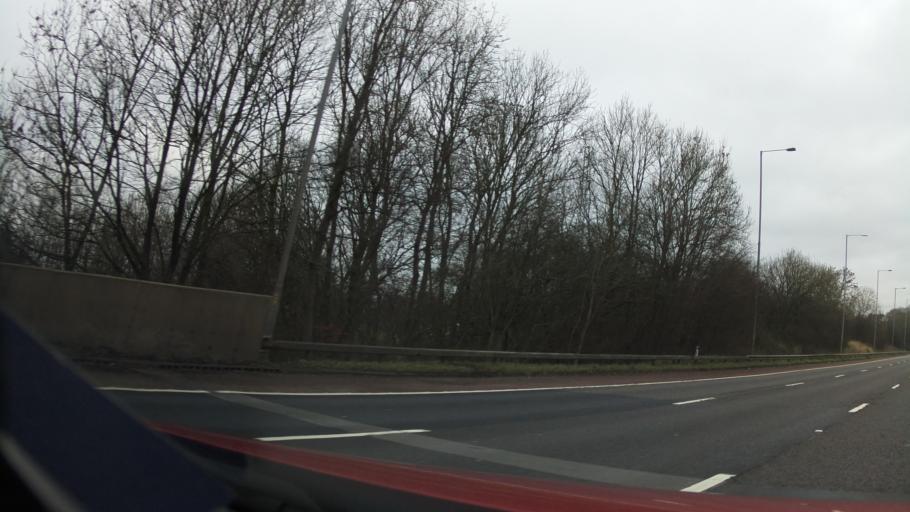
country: GB
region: England
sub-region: Lancashire
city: Euxton
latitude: 53.6551
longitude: -2.6912
